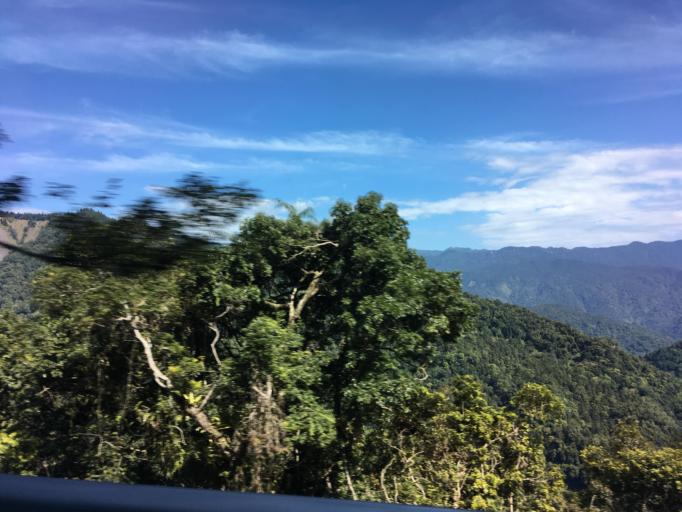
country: TW
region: Taiwan
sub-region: Yilan
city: Yilan
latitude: 24.5413
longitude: 121.5103
